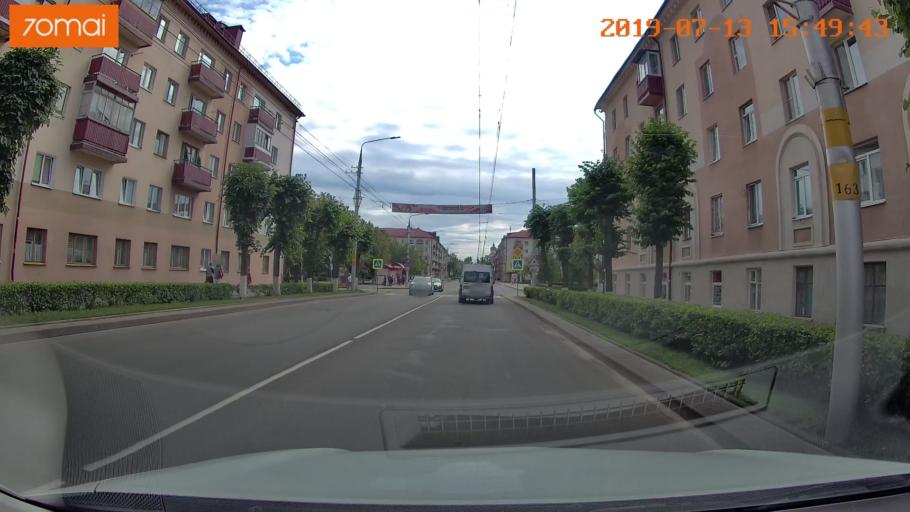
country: BY
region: Mogilev
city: Babruysk
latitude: 53.1459
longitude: 29.2279
